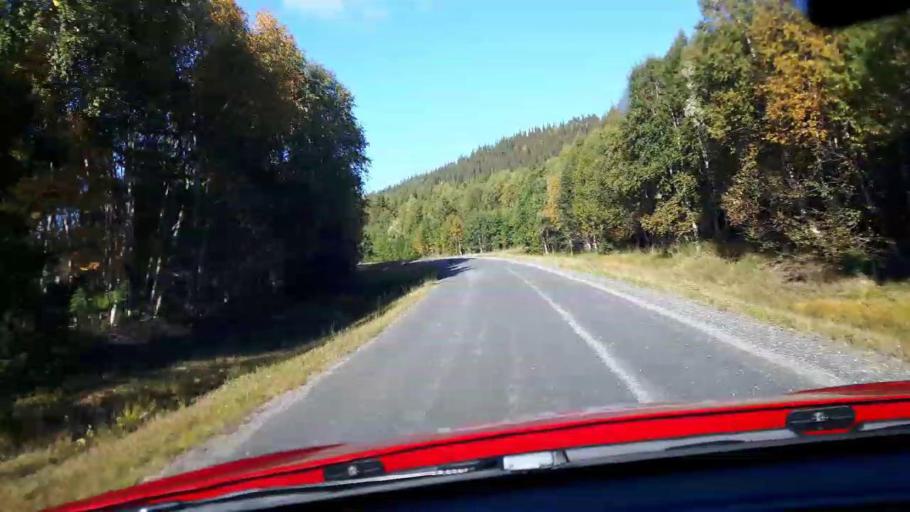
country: NO
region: Nord-Trondelag
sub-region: Lierne
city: Sandvika
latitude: 64.5905
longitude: 13.8557
